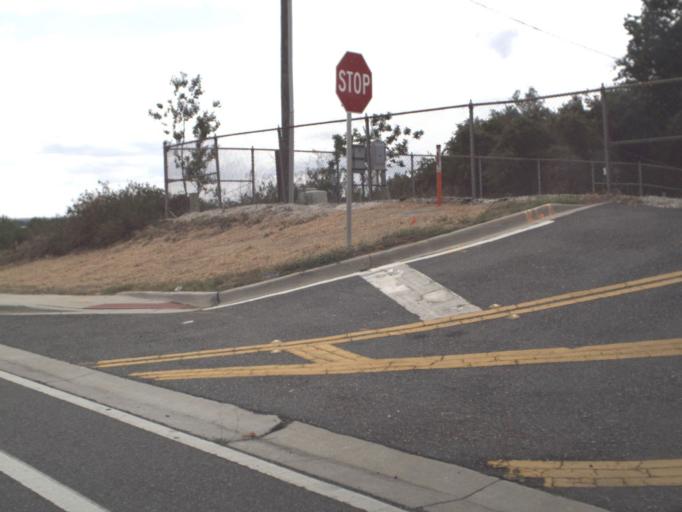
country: US
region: Florida
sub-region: Lake County
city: Minneola
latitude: 28.5469
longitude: -81.7191
